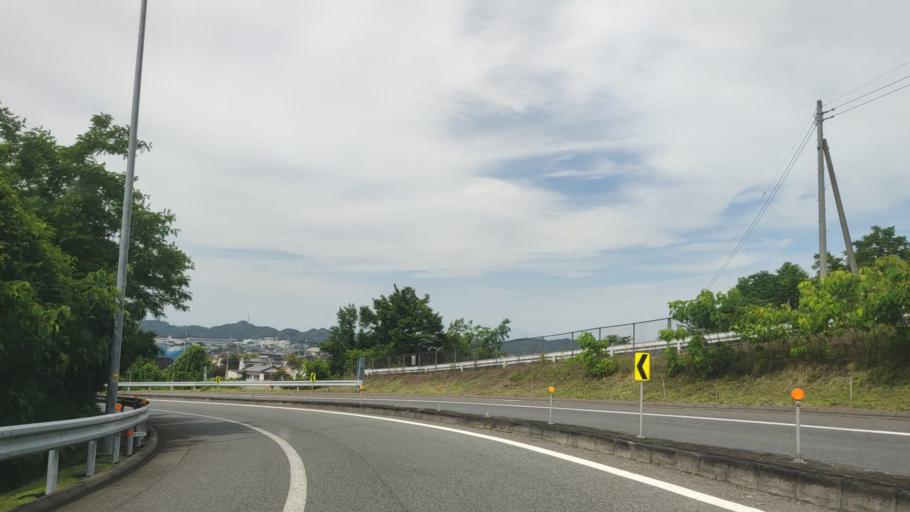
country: JP
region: Gunma
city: Tomioka
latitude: 36.2437
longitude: 138.8942
